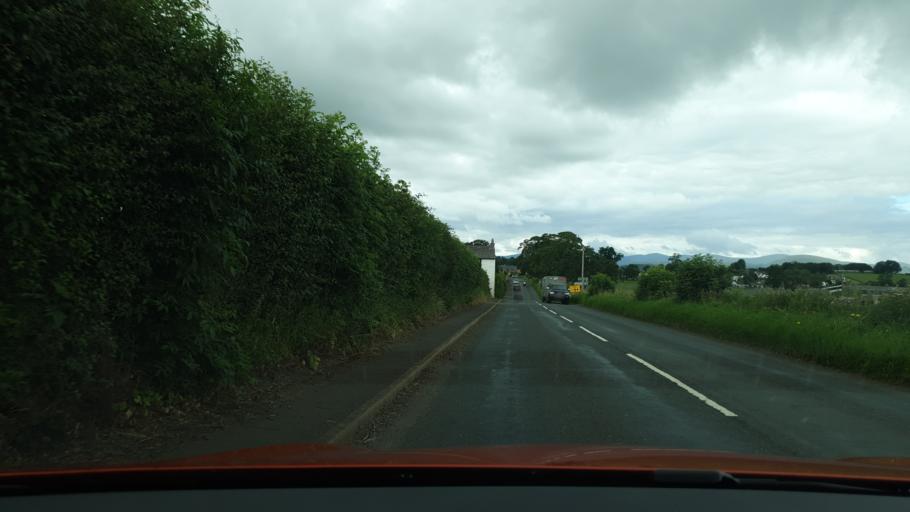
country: GB
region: England
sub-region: Cumbria
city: Penrith
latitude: 54.6371
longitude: -2.7637
